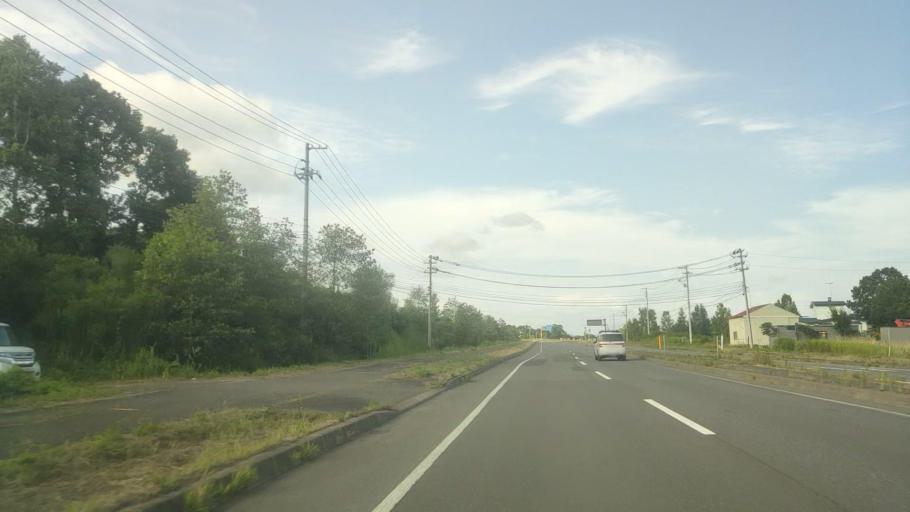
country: JP
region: Hokkaido
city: Chitose
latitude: 42.7724
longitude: 141.8256
